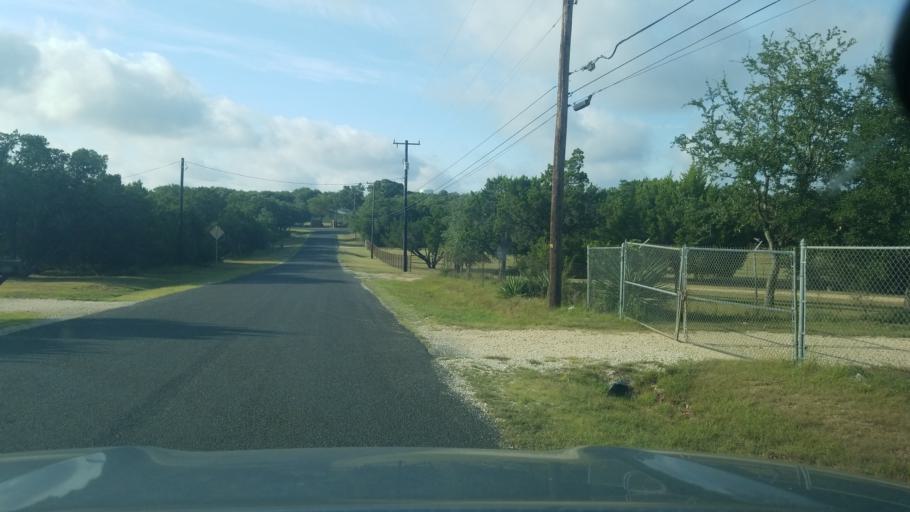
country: US
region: Texas
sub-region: Bexar County
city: Timberwood Park
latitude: 29.6968
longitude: -98.5155
